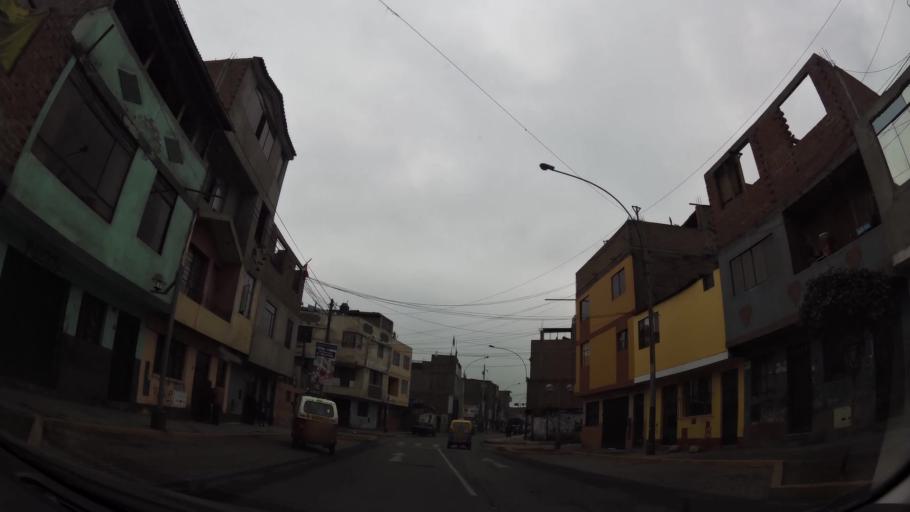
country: PE
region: Lima
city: Lima
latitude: -12.0509
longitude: -77.0055
